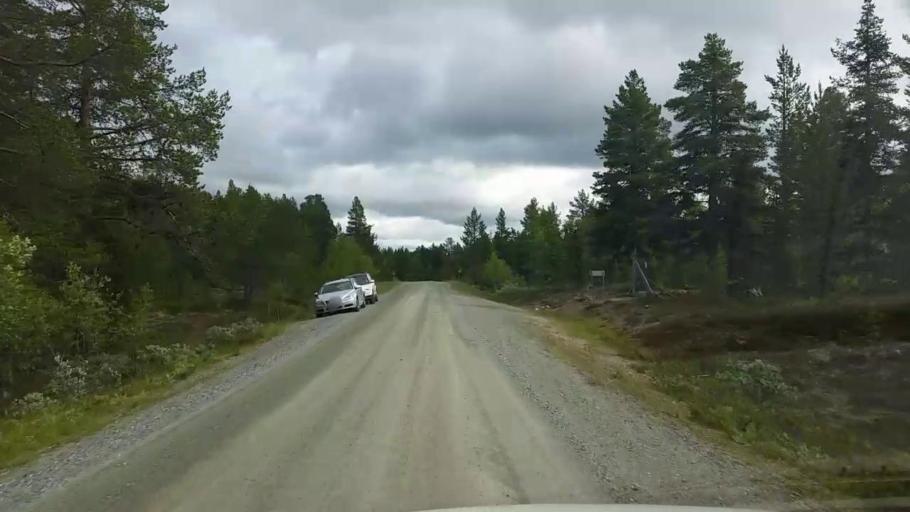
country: NO
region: Hedmark
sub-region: Engerdal
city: Engerdal
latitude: 62.3327
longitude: 12.6383
